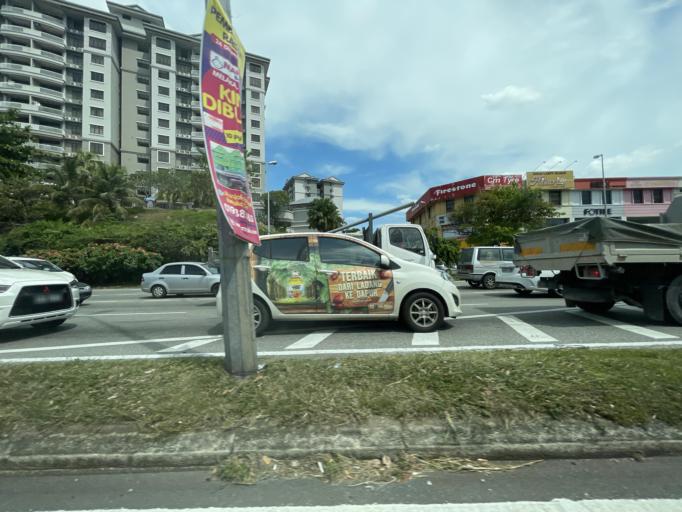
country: MY
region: Melaka
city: Batu Berendam
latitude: 2.2465
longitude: 102.2231
